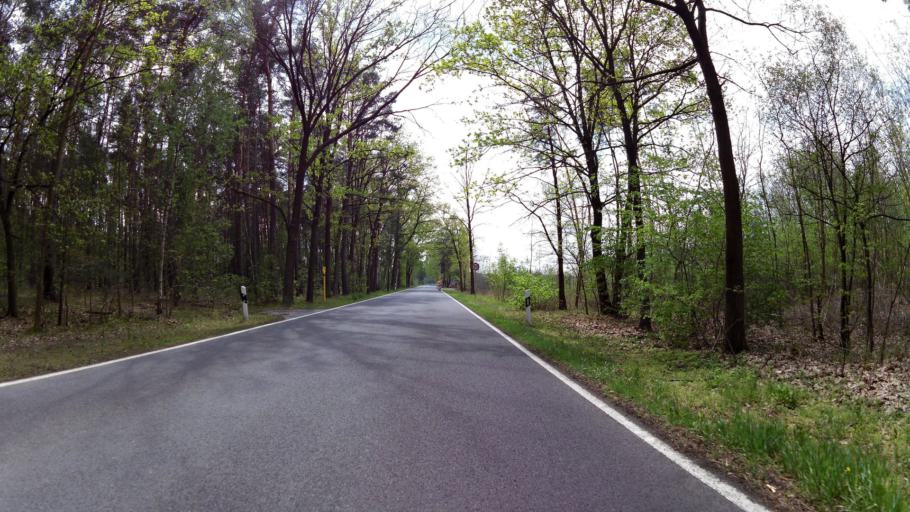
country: DE
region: Brandenburg
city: Bestensee
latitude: 52.2722
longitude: 13.7337
